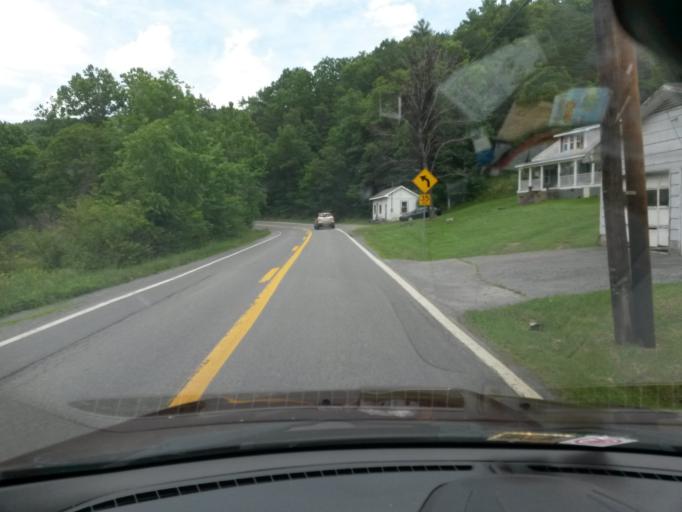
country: US
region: West Virginia
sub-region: Monroe County
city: Union
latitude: 37.4948
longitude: -80.6051
